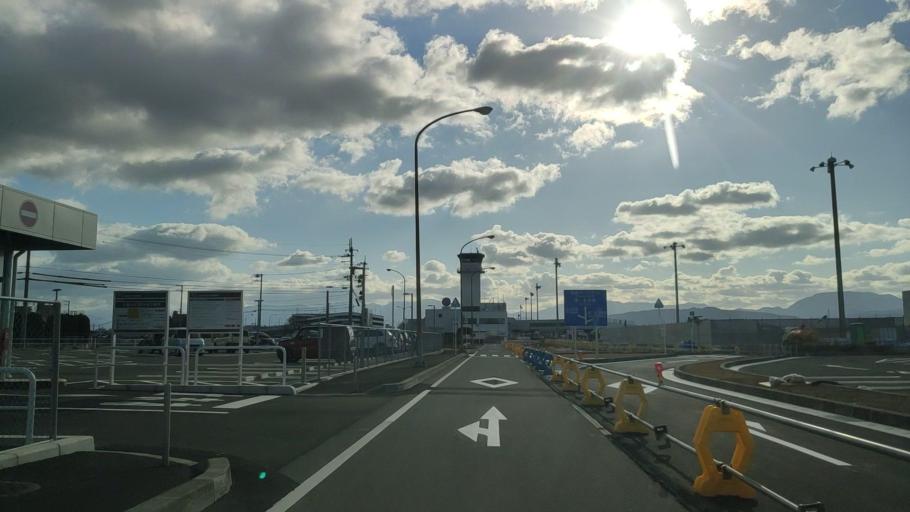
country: JP
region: Ehime
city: Masaki-cho
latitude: 33.8312
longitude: 132.7007
